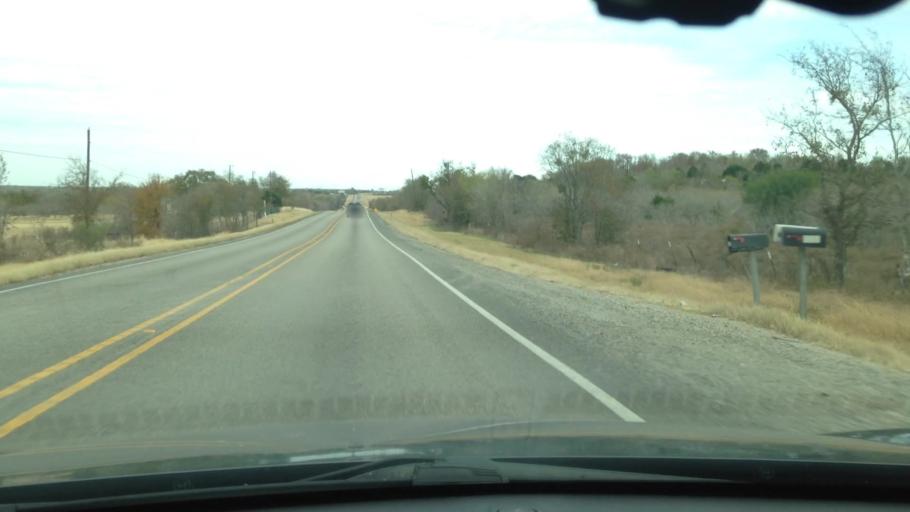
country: US
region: Texas
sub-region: Caldwell County
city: Uhland
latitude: 29.9738
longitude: -97.7697
